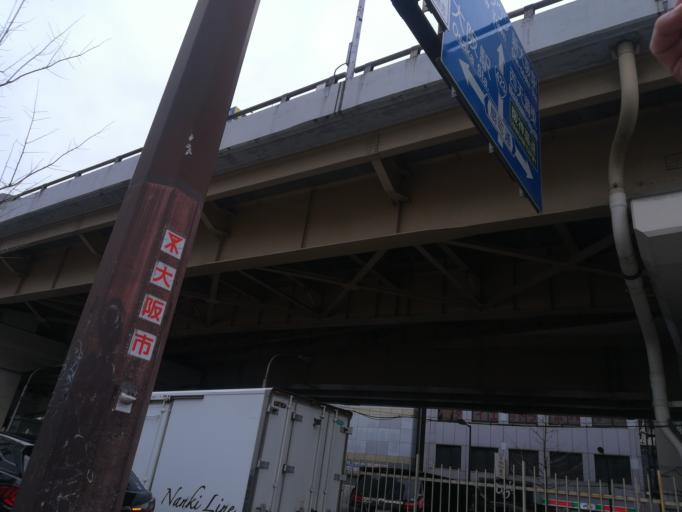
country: JP
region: Osaka
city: Osaka-shi
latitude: 34.7012
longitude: 135.5018
